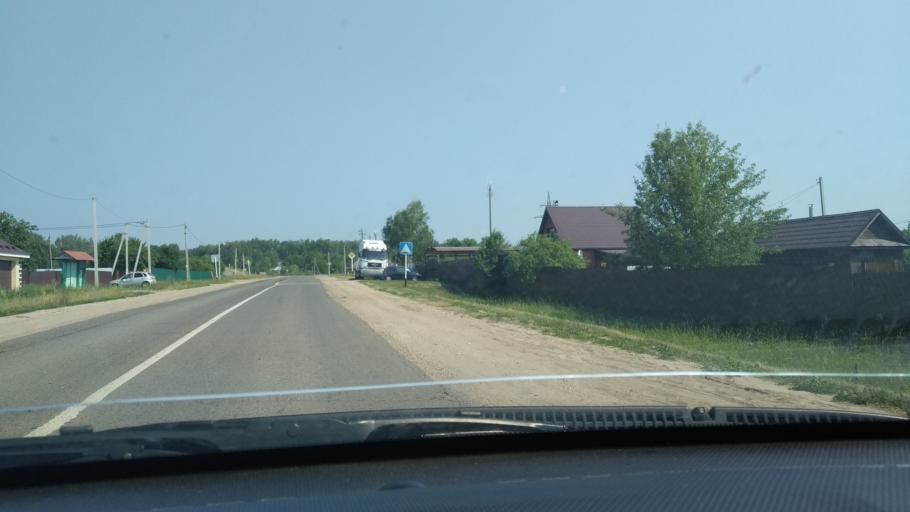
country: RU
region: Tatarstan
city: Osinovo
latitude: 55.9842
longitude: 48.8129
